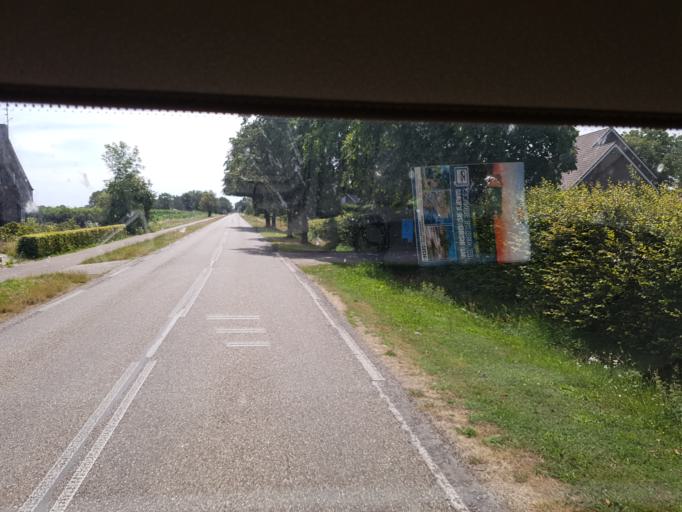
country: NL
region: Limburg
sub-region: Gemeente Leudal
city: Kelpen-Oler
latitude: 51.2151
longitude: 5.7992
